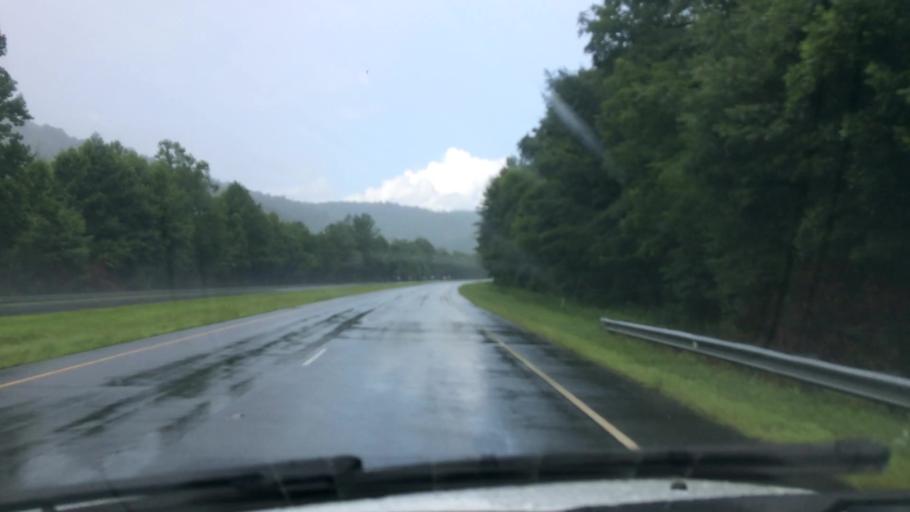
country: US
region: North Carolina
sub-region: Wilkes County
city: Millers Creek
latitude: 36.1936
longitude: -81.4188
